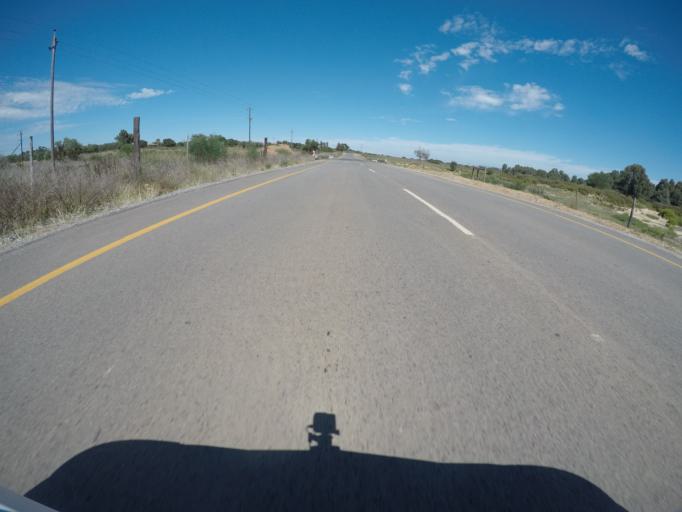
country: ZA
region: Western Cape
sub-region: West Coast District Municipality
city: Malmesbury
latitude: -33.5828
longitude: 18.6468
